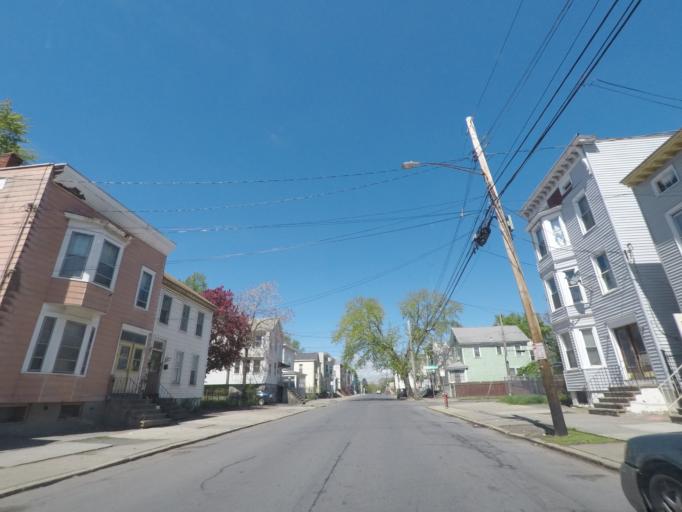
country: US
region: New York
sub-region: Albany County
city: Albany
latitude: 42.6643
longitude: -73.7597
